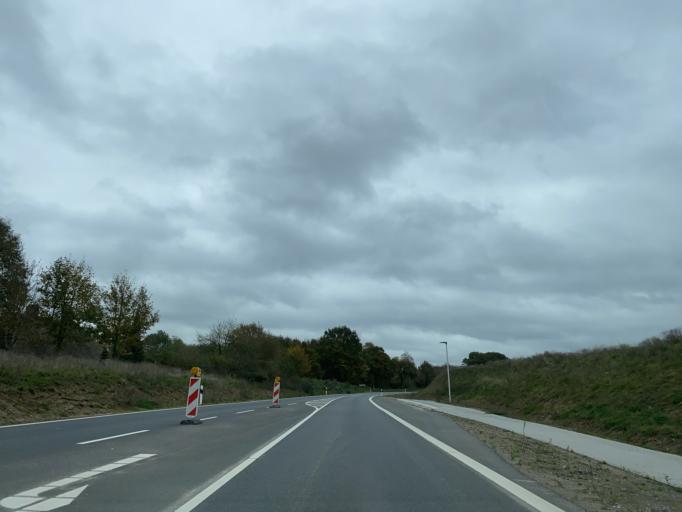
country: DE
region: Schleswig-Holstein
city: Tastrup
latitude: 54.7774
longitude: 9.4906
